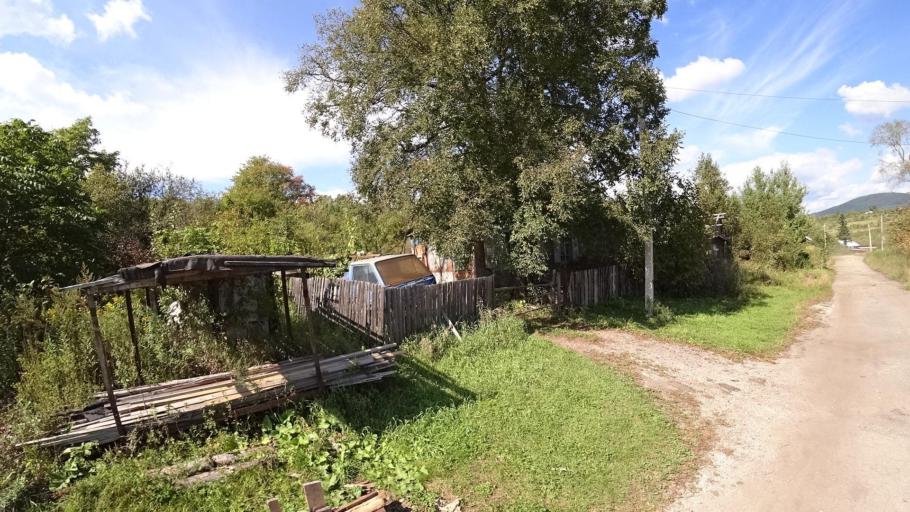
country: RU
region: Jewish Autonomous Oblast
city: Birakan
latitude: 48.9997
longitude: 131.8522
